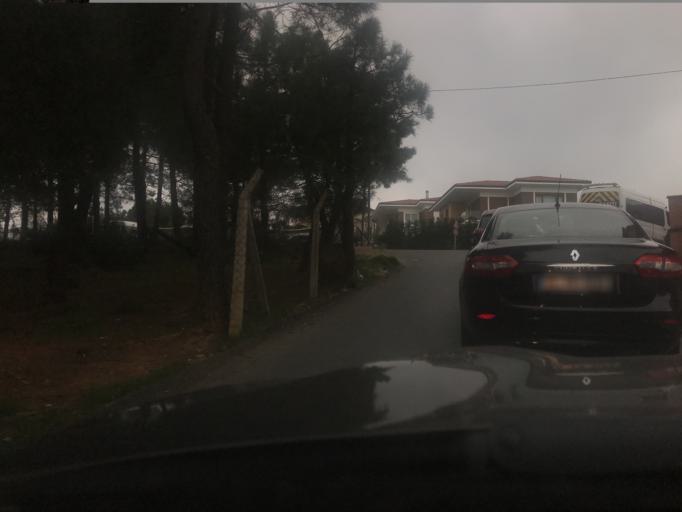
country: TR
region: Istanbul
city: Umraniye
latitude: 41.0507
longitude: 29.1728
